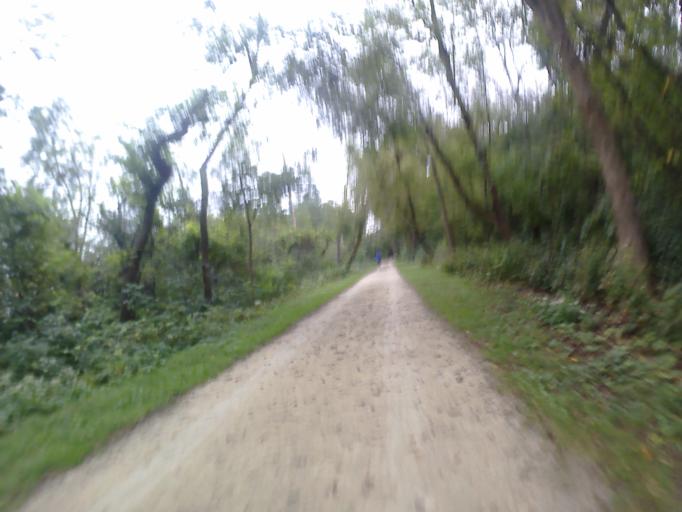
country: US
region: Illinois
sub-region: DuPage County
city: Wheaton
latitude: 41.8493
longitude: -88.1202
